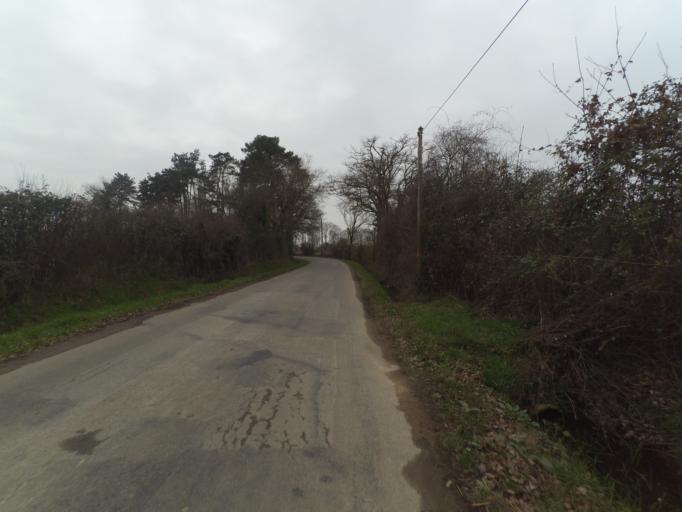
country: FR
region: Pays de la Loire
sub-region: Departement de la Loire-Atlantique
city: Sautron
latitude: 47.2582
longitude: -1.7072
